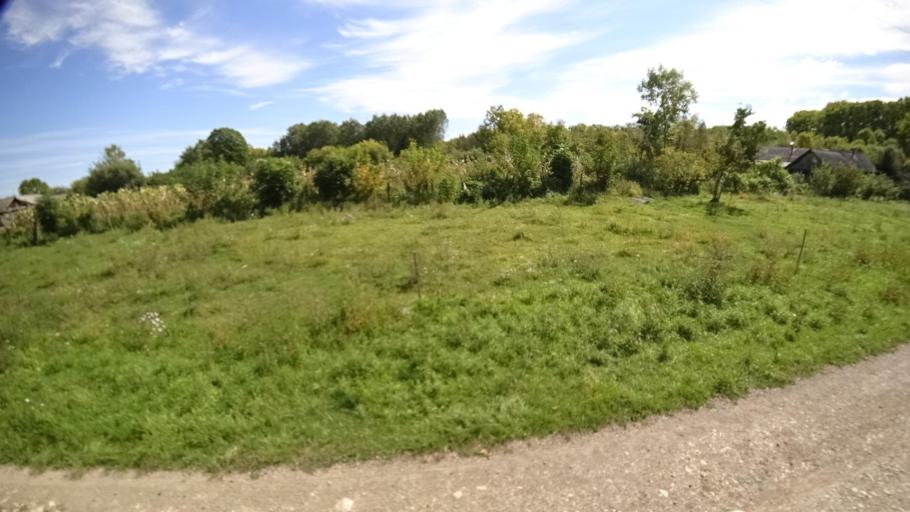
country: RU
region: Primorskiy
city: Kirovskiy
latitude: 44.7583
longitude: 133.6113
